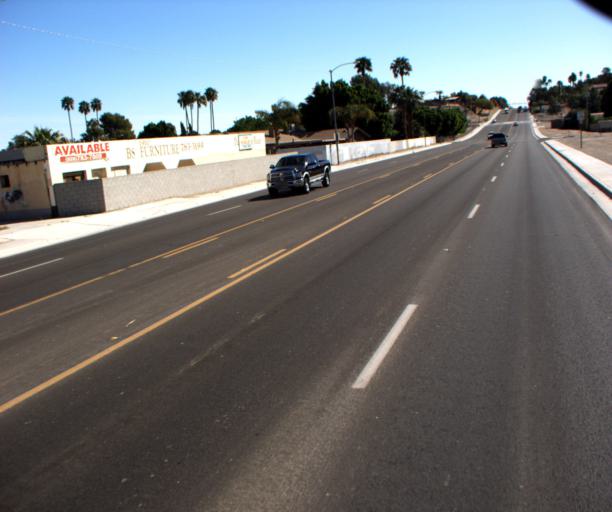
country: US
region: Arizona
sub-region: Yuma County
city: Yuma
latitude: 32.6984
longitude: -114.6446
